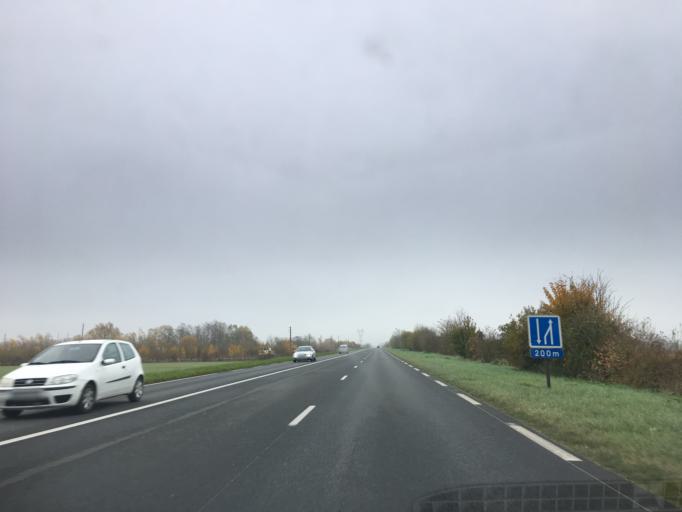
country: FR
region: Ile-de-France
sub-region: Departement de Seine-et-Marne
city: La Grande-Paroisse
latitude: 48.3611
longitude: 2.9023
